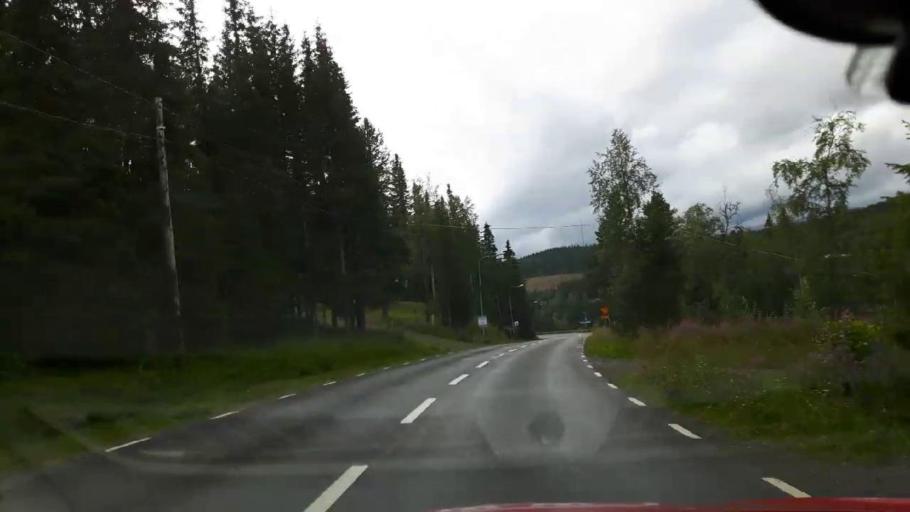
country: NO
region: Nord-Trondelag
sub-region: Lierne
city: Sandvika
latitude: 64.4983
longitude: 14.1501
